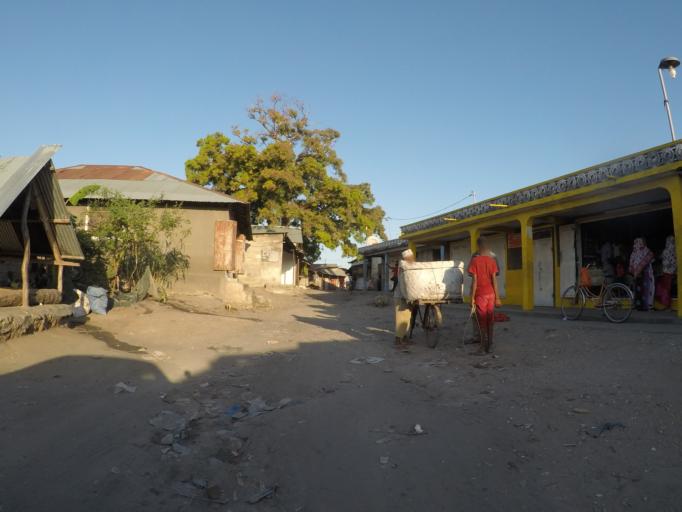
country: TZ
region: Zanzibar Urban/West
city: Zanzibar
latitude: -6.1583
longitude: 39.2172
